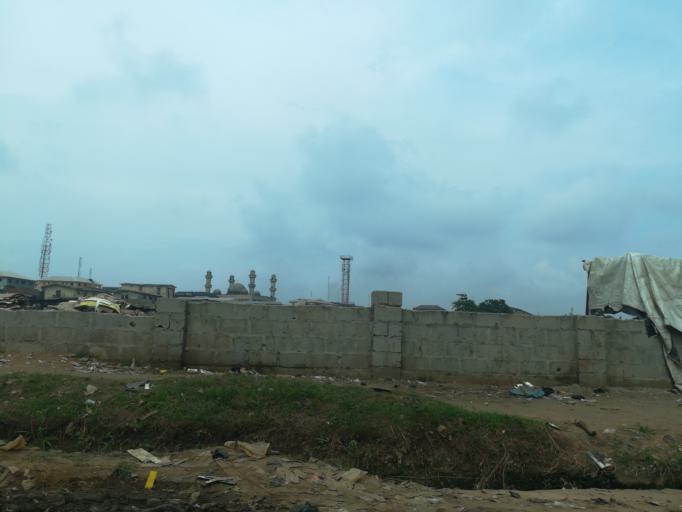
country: NG
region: Lagos
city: Ikorodu
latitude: 6.6214
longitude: 3.5070
